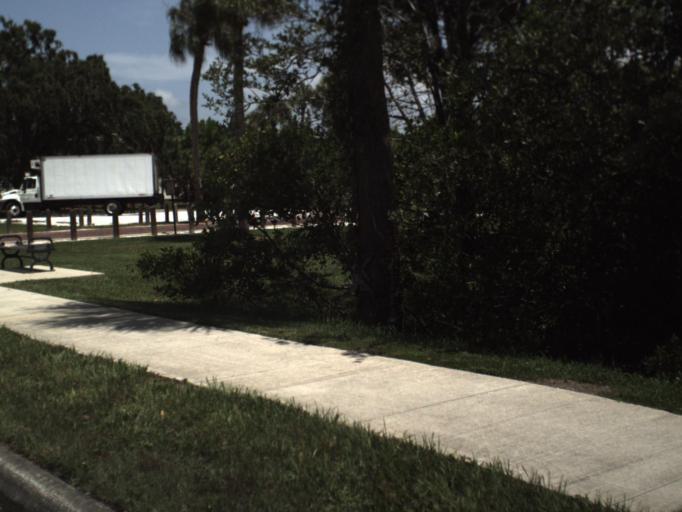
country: US
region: Florida
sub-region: Pinellas County
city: Dunedin
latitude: 28.0206
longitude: -82.7896
